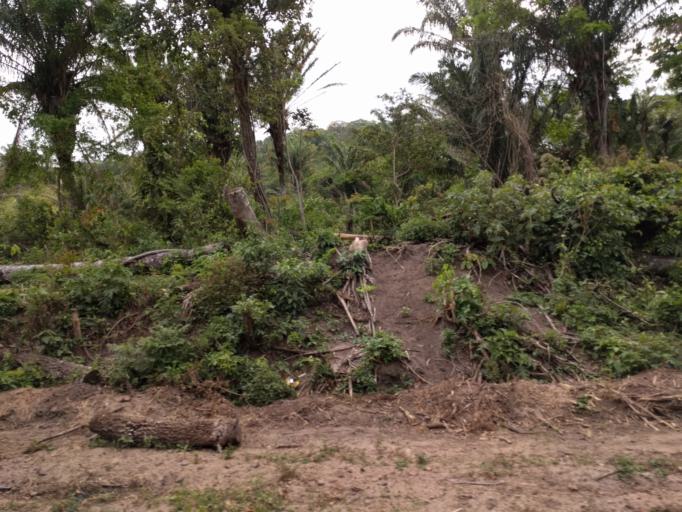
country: BO
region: Santa Cruz
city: Santiago del Torno
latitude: -17.9059
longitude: -63.4364
